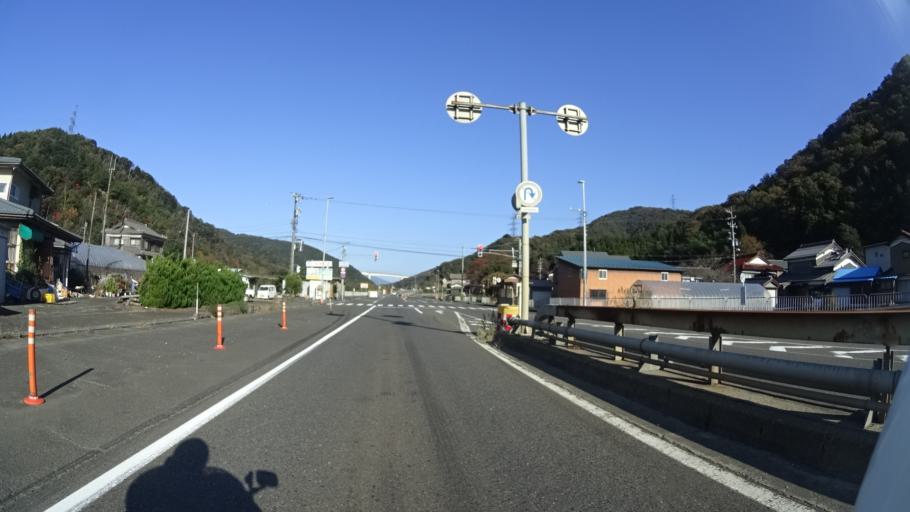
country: JP
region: Fukui
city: Tsuruga
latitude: 35.6112
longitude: 136.0852
